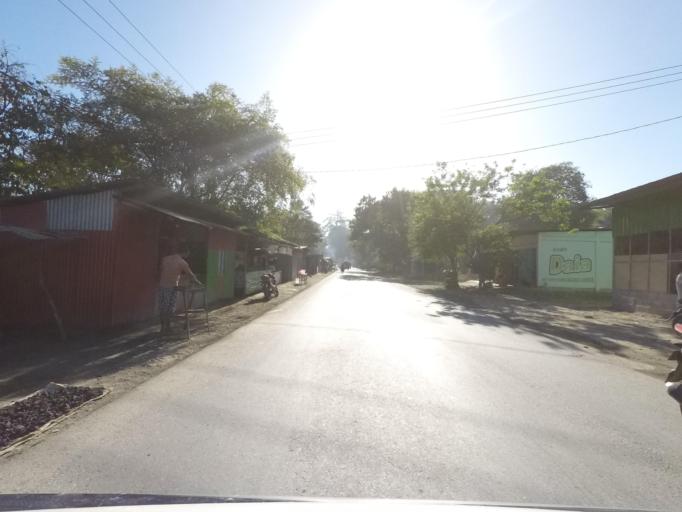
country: ID
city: Metinaro
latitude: -8.5508
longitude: 125.6626
